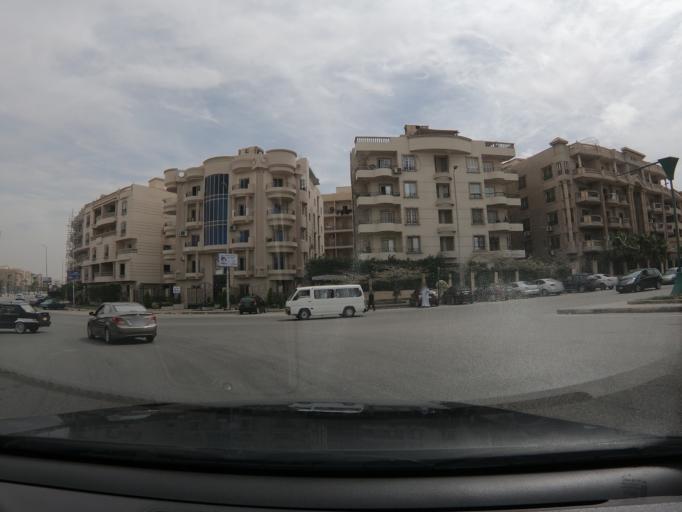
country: EG
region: Muhafazat al Qahirah
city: Cairo
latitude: 30.0073
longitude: 31.4116
